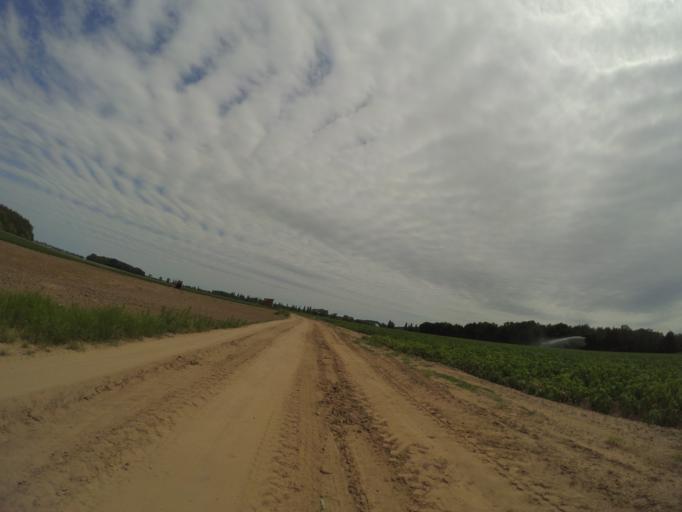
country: CZ
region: Central Bohemia
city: Prerov nad Labem
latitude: 50.1826
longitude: 14.8150
